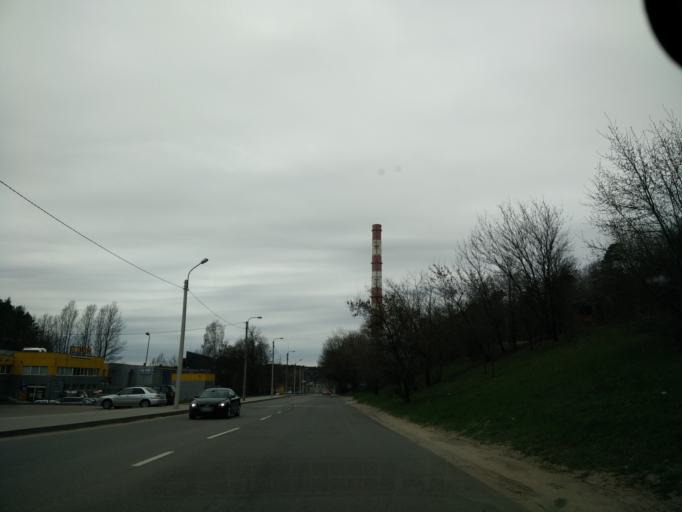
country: LT
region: Vilnius County
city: Vilkpede
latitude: 54.6634
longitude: 25.2411
